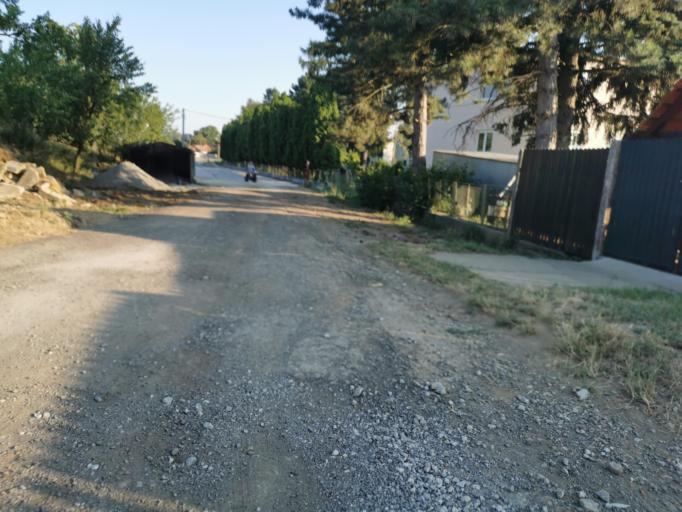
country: SK
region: Trnavsky
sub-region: Okres Skalica
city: Skalica
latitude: 48.7760
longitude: 17.2796
